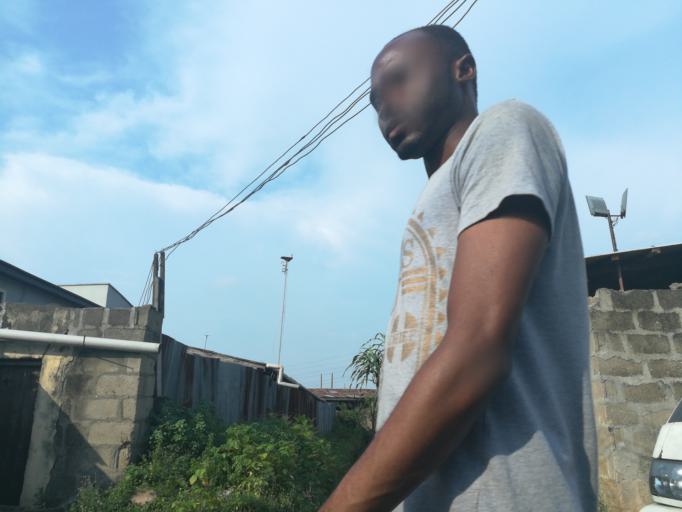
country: NG
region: Lagos
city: Ojota
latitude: 6.5930
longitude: 3.3987
